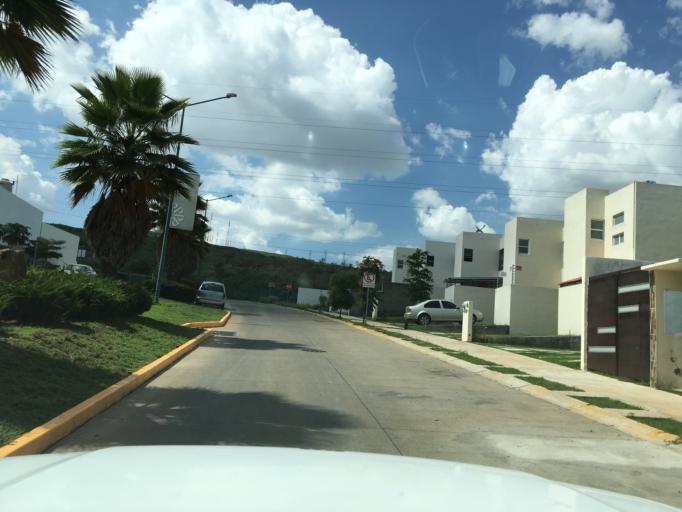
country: MX
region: Jalisco
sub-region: Tlajomulco de Zuniga
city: Altus Bosques
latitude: 20.5854
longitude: -103.3649
